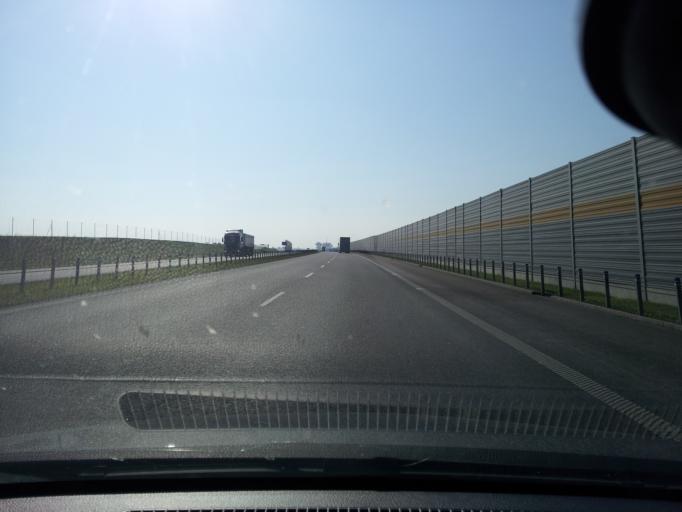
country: PL
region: Kujawsko-Pomorskie
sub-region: Powiat torunski
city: Lubicz Dolny
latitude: 53.1239
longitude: 18.7398
